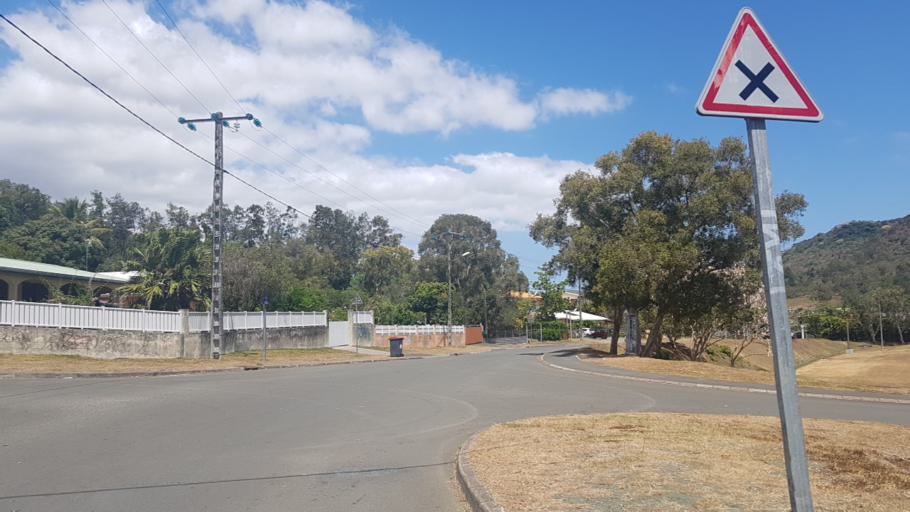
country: NC
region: South Province
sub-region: Dumbea
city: Dumbea
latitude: -22.1340
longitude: 166.4321
